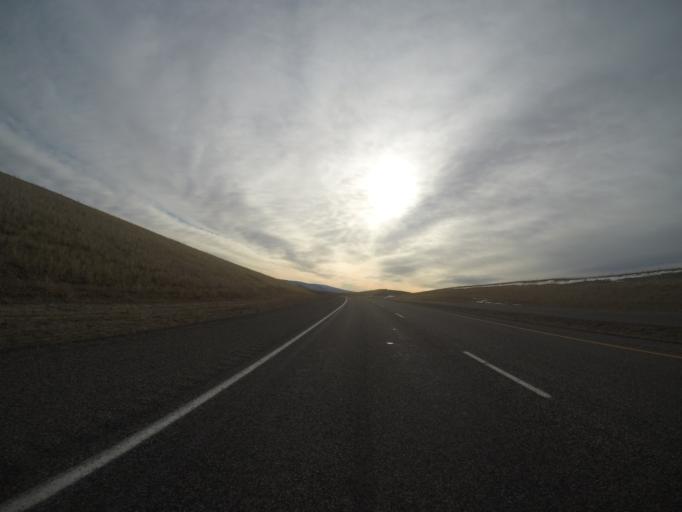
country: US
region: Montana
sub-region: Yellowstone County
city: Laurel
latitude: 45.5474
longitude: -108.8622
